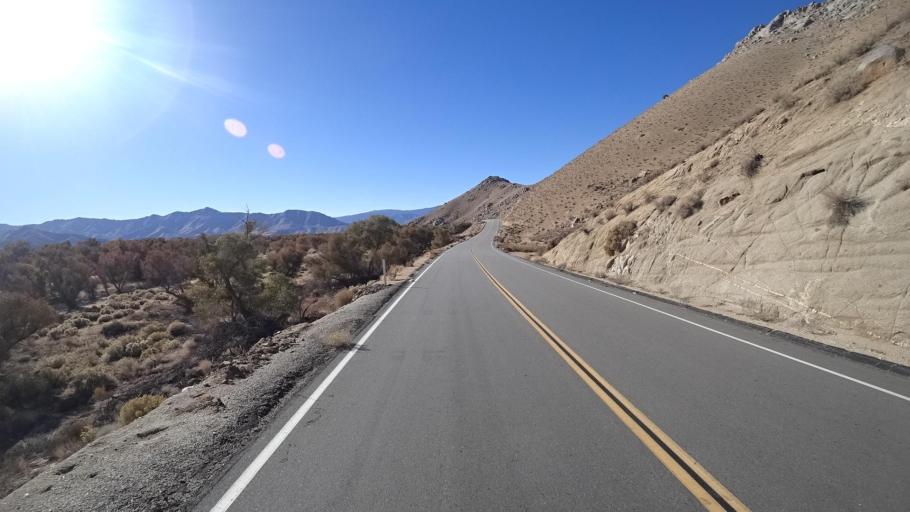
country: US
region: California
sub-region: Kern County
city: Weldon
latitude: 35.6723
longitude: -118.3494
